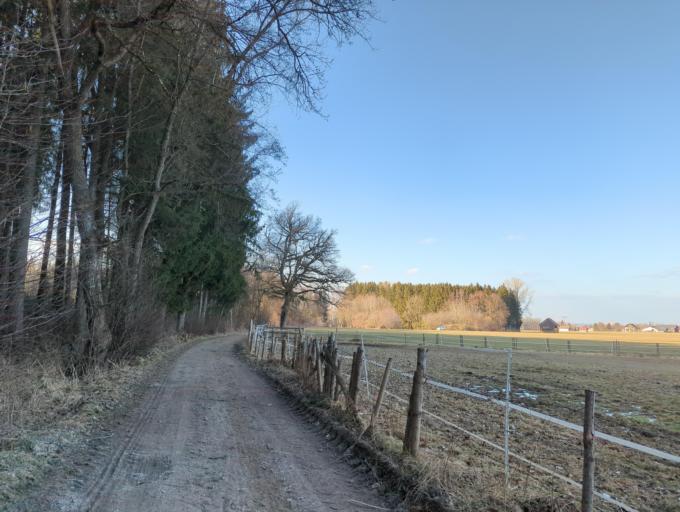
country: DE
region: Bavaria
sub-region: Swabia
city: Bad Worishofen
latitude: 47.9873
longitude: 10.5904
